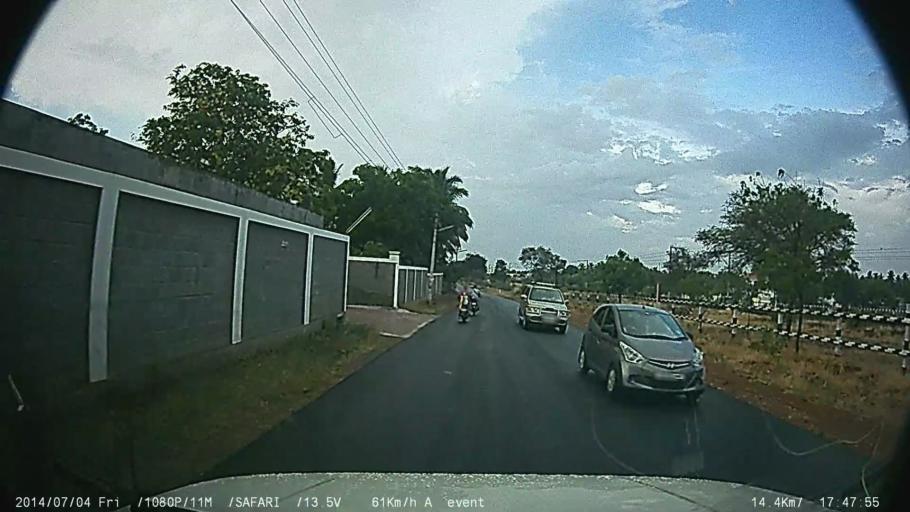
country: IN
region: Tamil Nadu
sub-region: Tiruppur
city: Tiruppur
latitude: 11.1107
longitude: 77.3047
